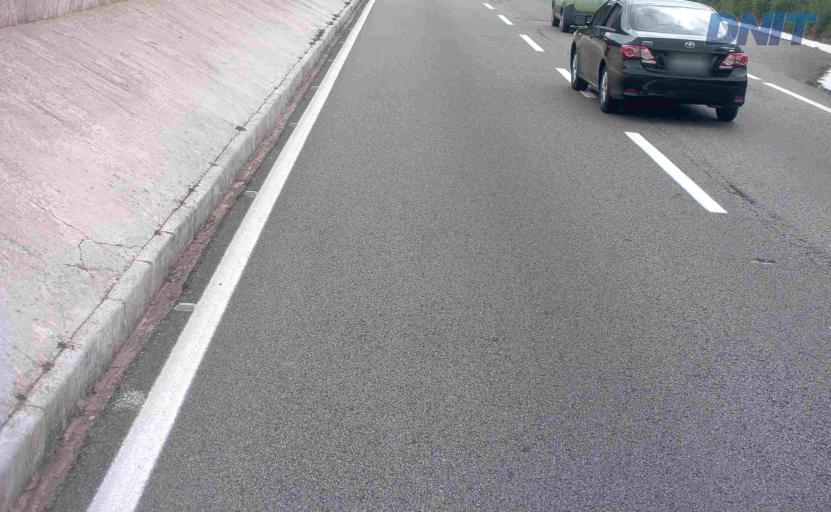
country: BR
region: Minas Gerais
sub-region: Caete
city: Caete
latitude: -19.7907
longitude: -43.6816
